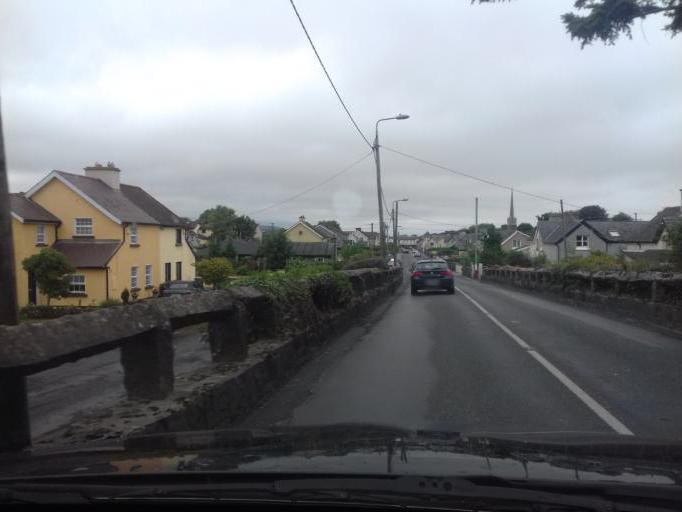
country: IE
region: Leinster
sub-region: County Carlow
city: Bagenalstown
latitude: 52.6976
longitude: -6.9571
